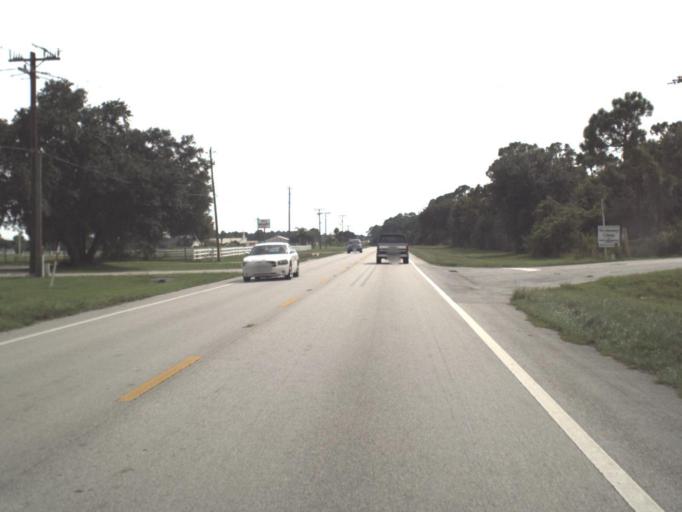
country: US
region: Florida
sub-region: Okeechobee County
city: Cypress Quarters
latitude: 27.2879
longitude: -80.8284
